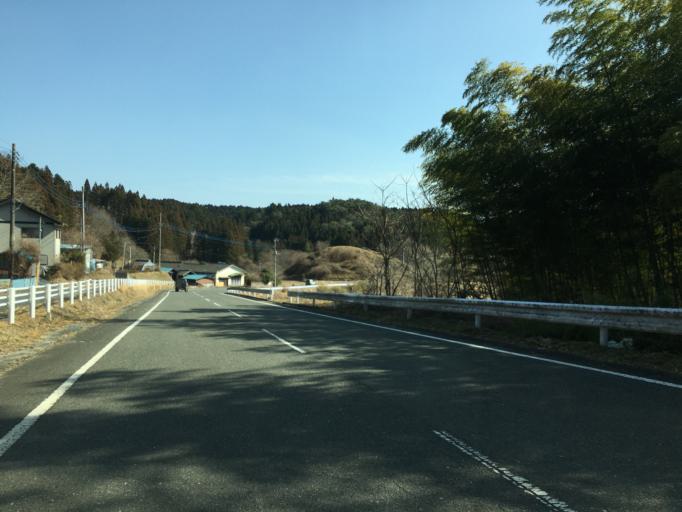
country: JP
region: Ibaraki
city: Kitaibaraki
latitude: 36.8267
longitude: 140.5714
